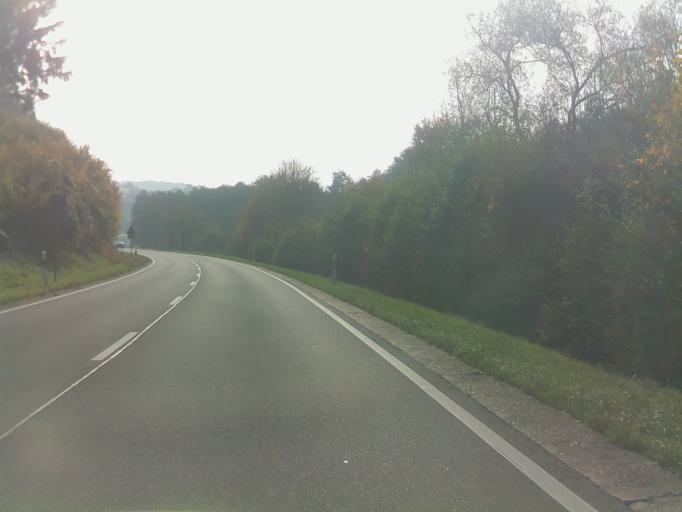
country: DE
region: Baden-Wuerttemberg
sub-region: Karlsruhe Region
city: Limbach
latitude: 49.4079
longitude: 9.2356
